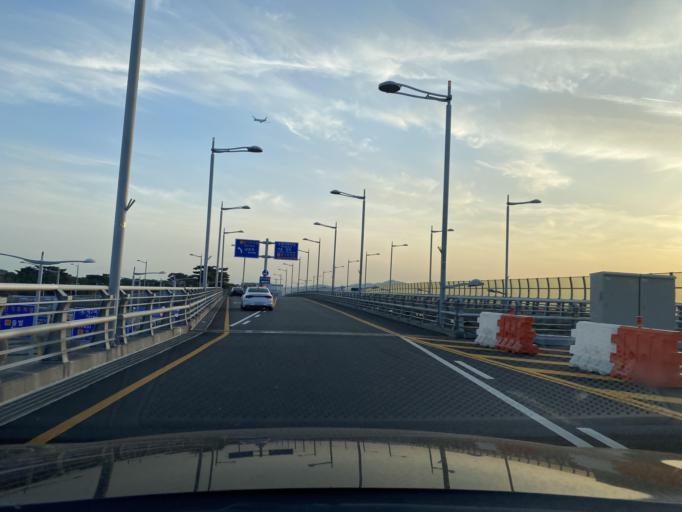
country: KR
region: Incheon
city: Incheon
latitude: 37.4462
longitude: 126.4498
